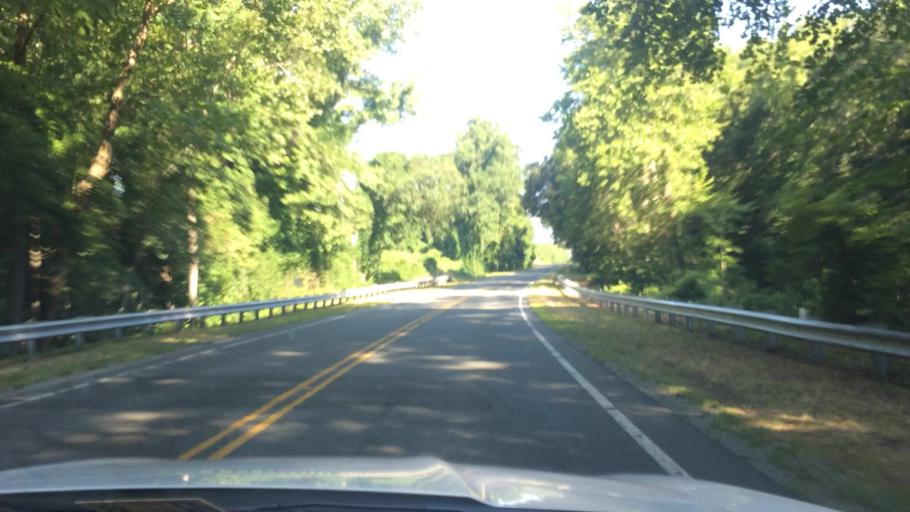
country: US
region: Virginia
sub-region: Lancaster County
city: Lancaster
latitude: 37.8000
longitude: -76.5294
